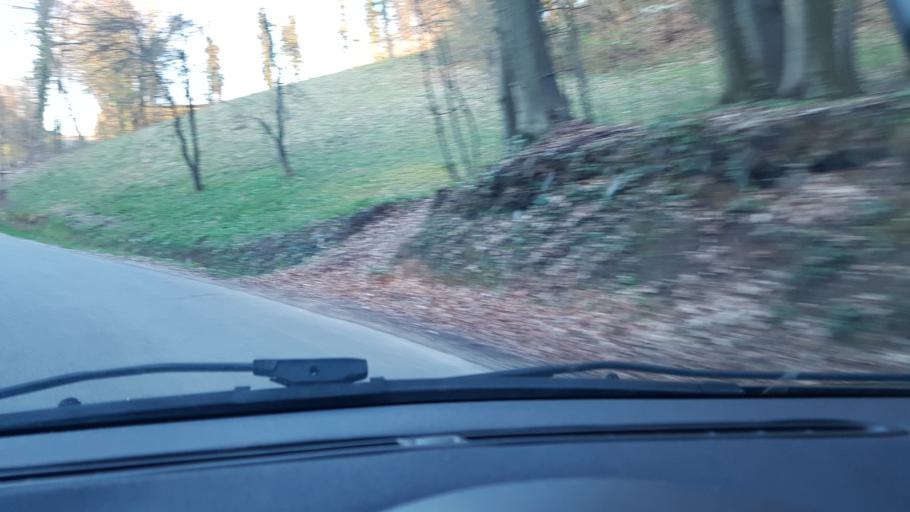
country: SI
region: Rogatec
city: Rogatec
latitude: 46.1839
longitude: 15.6796
